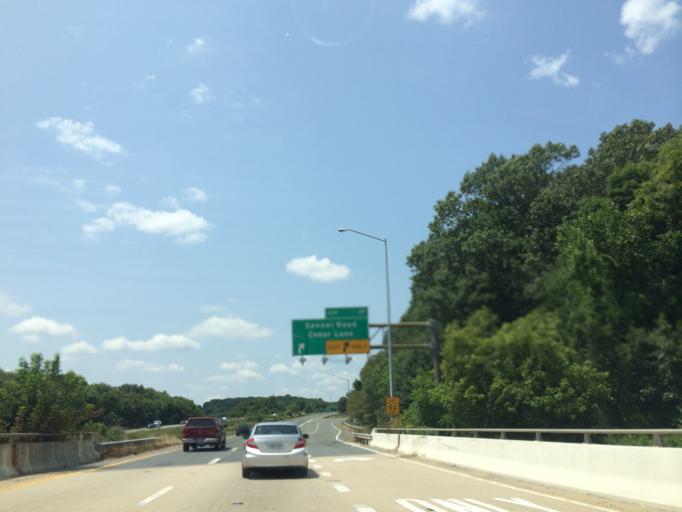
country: US
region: Maryland
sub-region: Howard County
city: Riverside
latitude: 39.1837
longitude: -76.8908
